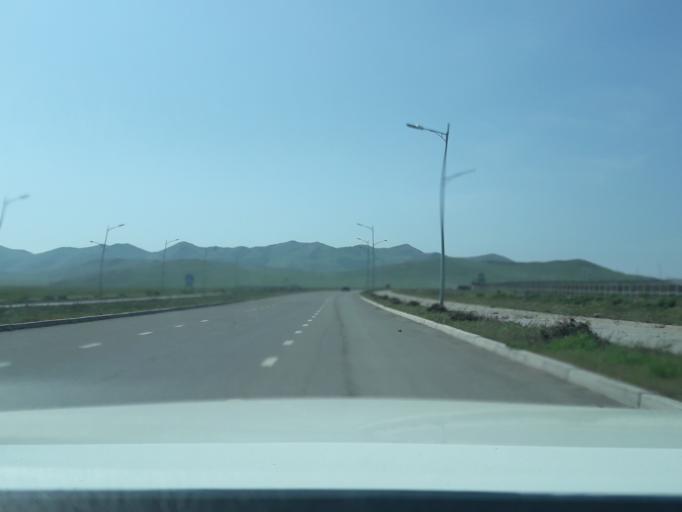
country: MN
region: Ulaanbaatar
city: Ulaanbaatar
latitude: 47.8324
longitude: 106.7868
